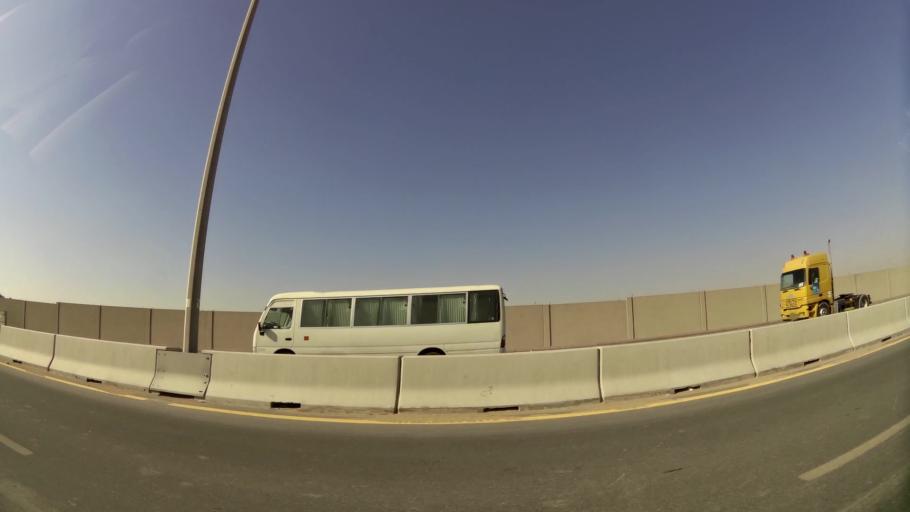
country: AE
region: Dubai
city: Dubai
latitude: 24.9876
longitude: 55.1156
